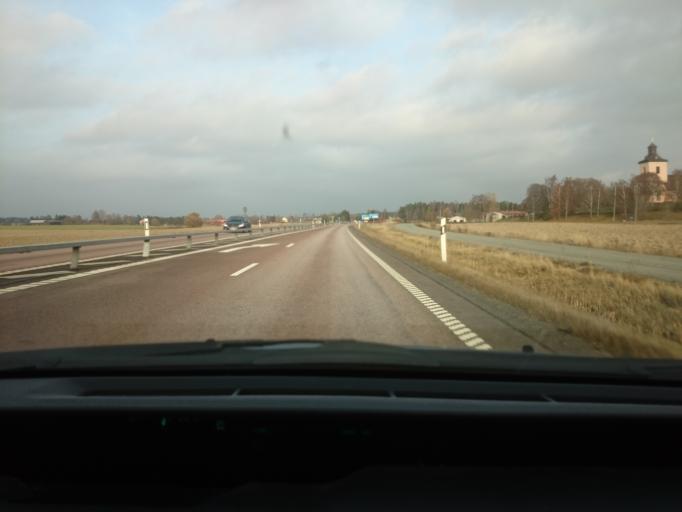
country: SE
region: Vaestmanland
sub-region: Sala Kommun
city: Sala
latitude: 59.8677
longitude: 16.5414
